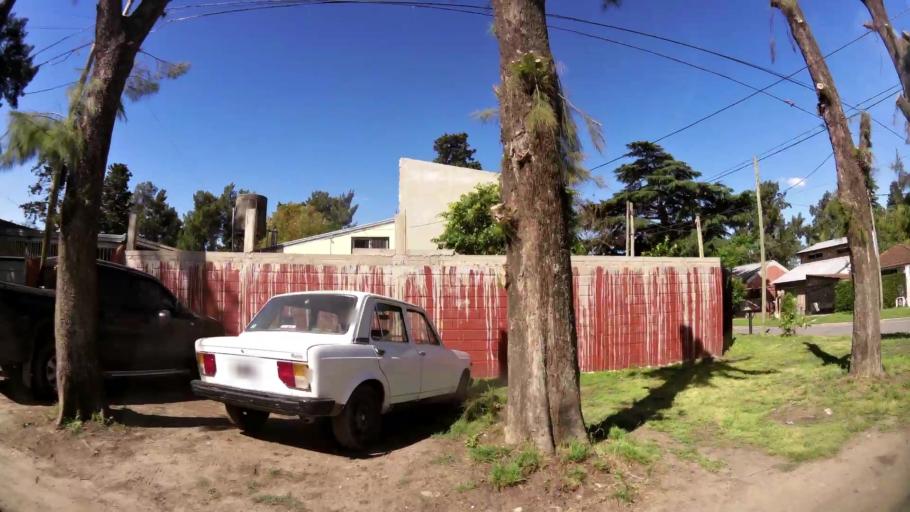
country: AR
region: Buenos Aires
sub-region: Partido de Almirante Brown
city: Adrogue
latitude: -34.7996
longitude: -58.3518
